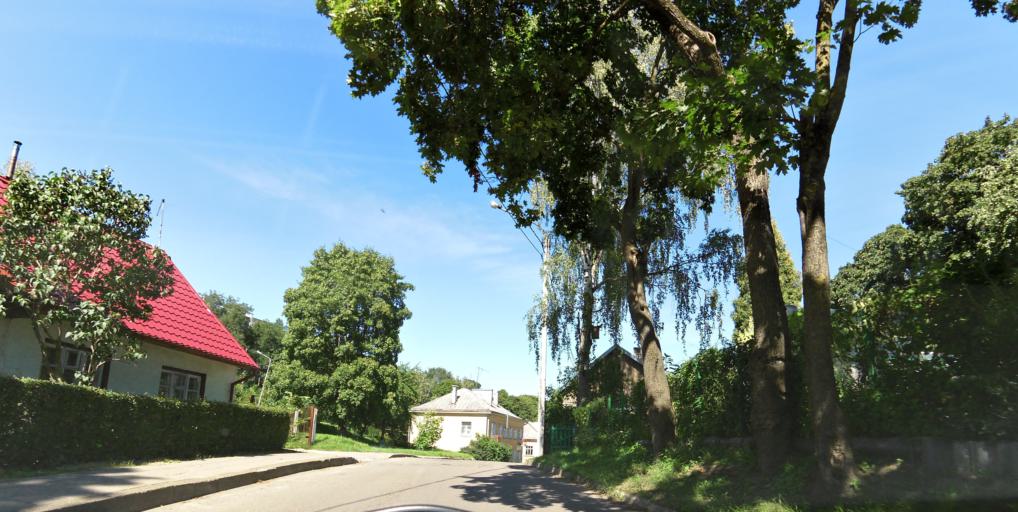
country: LT
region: Vilnius County
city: Naujamiestis
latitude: 54.6658
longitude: 25.2896
